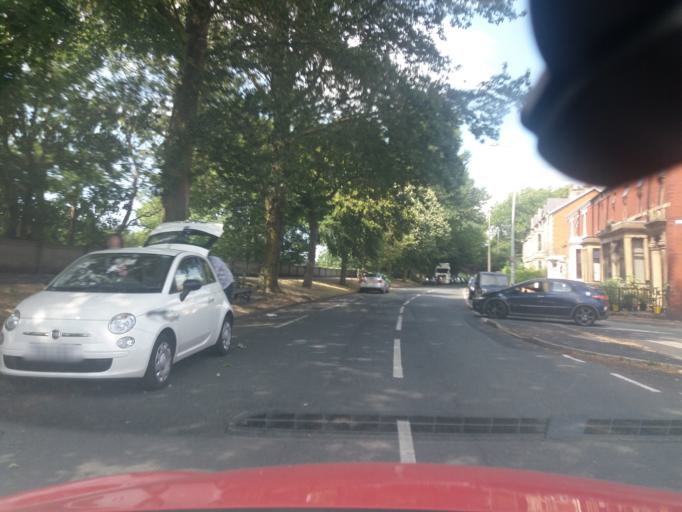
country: GB
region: England
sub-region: Lancashire
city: Preston
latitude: 53.7516
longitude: -2.7162
